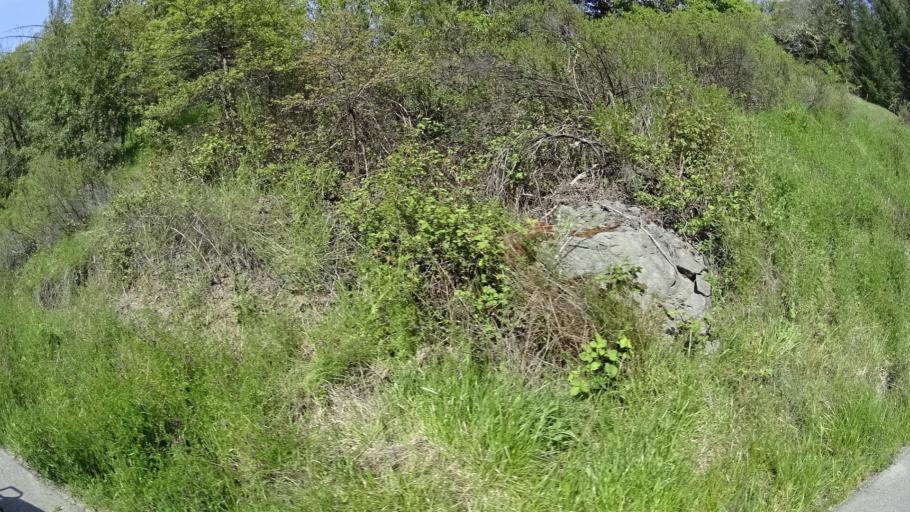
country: US
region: California
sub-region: Humboldt County
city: Redway
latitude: 40.3680
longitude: -123.7299
